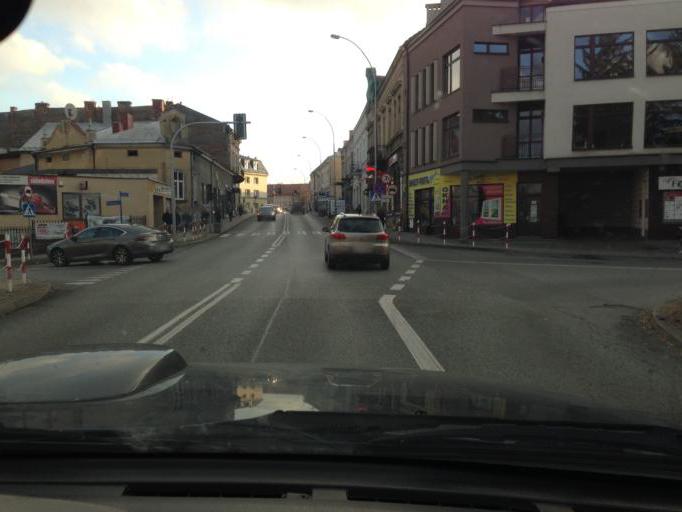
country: PL
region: Subcarpathian Voivodeship
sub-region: Powiat jasielski
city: Jaslo
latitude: 49.7490
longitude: 21.4732
